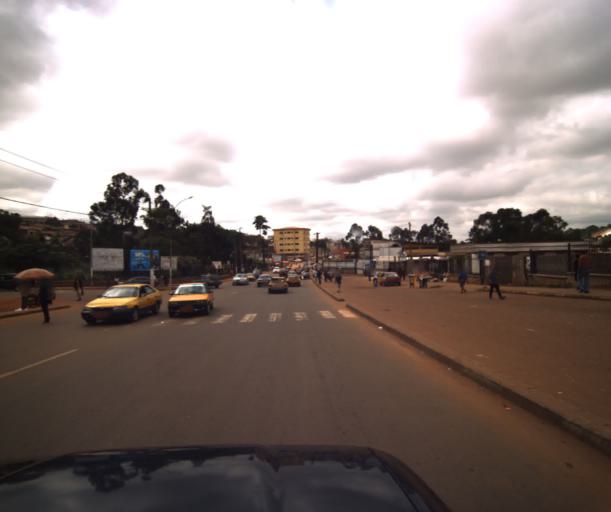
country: CM
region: Centre
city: Yaounde
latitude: 3.8593
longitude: 11.5218
